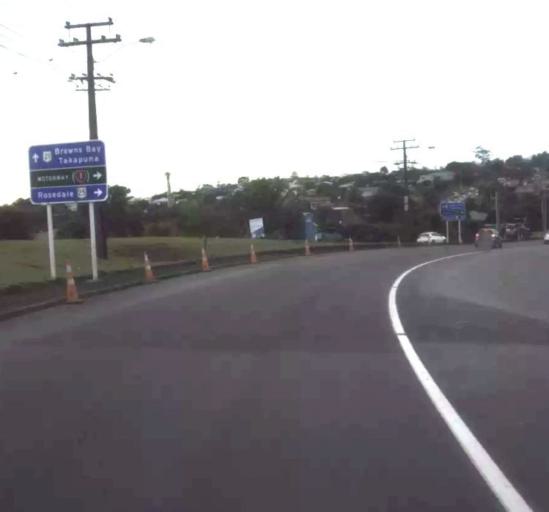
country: NZ
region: Auckland
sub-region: Auckland
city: Rothesay Bay
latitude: -36.7266
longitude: 174.7263
